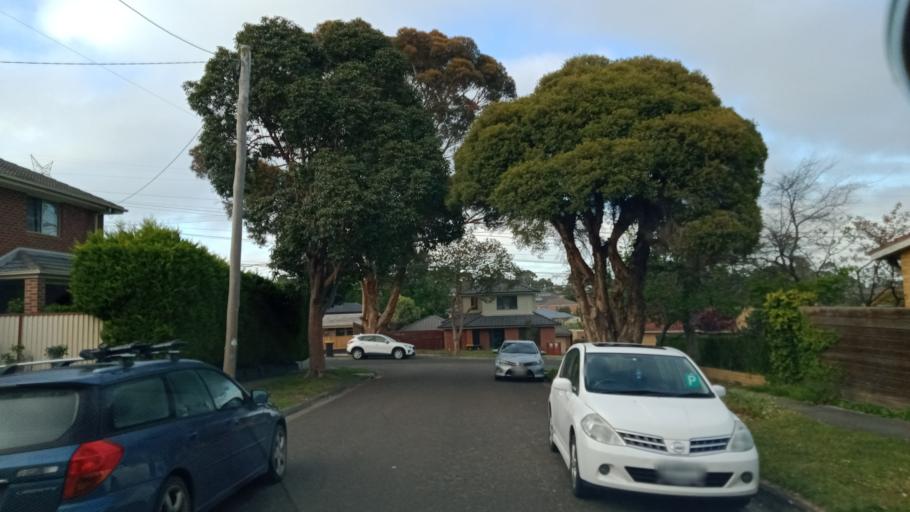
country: AU
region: Victoria
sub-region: Monash
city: Notting Hill
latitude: -37.8904
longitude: 145.1385
